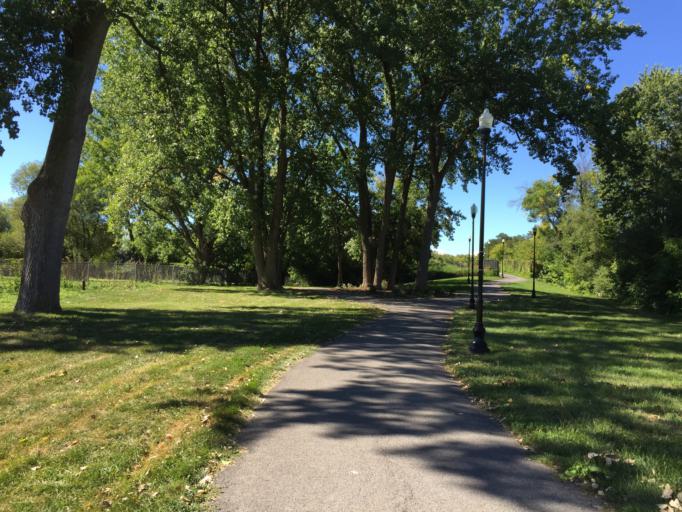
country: US
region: New York
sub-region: Onondaga County
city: Syracuse
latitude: 43.0626
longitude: -76.1704
